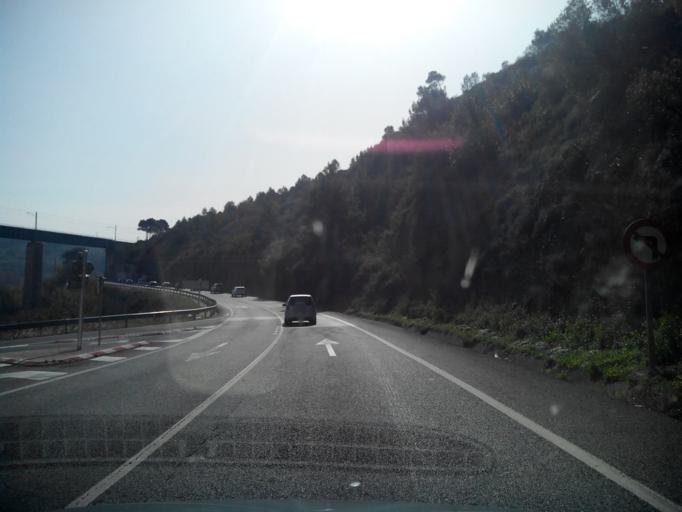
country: ES
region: Catalonia
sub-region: Provincia de Tarragona
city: Alcover
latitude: 41.3058
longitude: 1.1928
